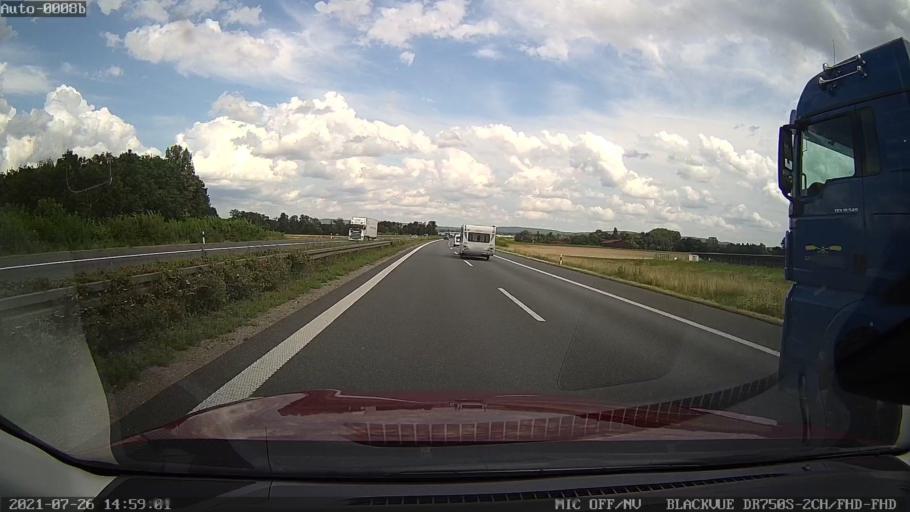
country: DE
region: Bavaria
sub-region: Regierungsbezirk Unterfranken
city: Kleinlangheim
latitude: 49.7814
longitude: 10.2712
